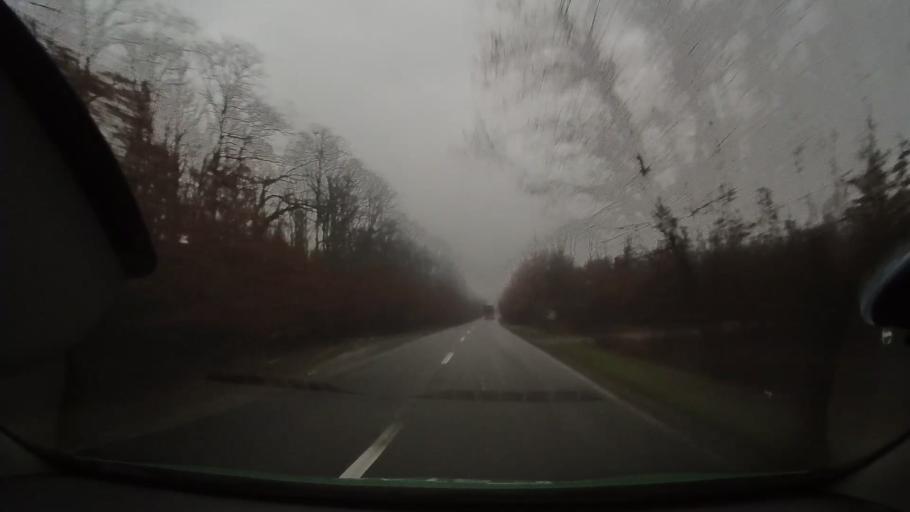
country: RO
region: Arad
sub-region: Comuna Beliu
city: Beliu
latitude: 46.5147
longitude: 21.9582
